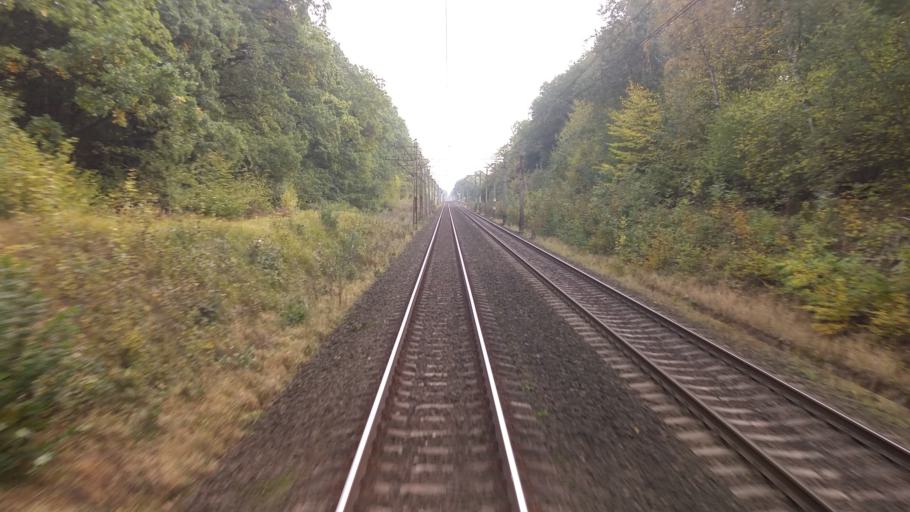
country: PL
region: West Pomeranian Voivodeship
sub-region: Powiat stargardzki
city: Dolice
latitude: 53.1886
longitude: 15.2480
